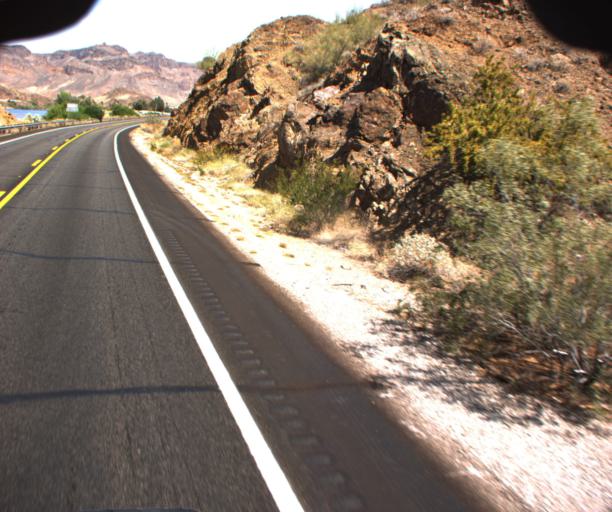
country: US
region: Arizona
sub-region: La Paz County
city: Cienega Springs
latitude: 34.2567
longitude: -114.1543
